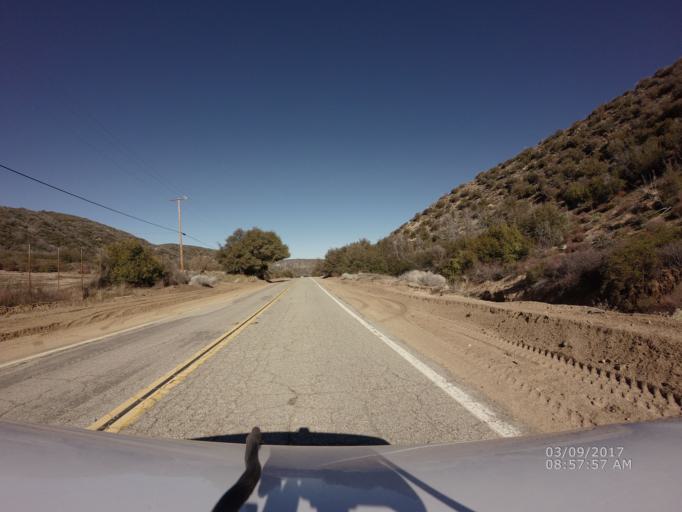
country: US
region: California
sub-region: Los Angeles County
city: Green Valley
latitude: 34.7247
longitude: -118.5863
